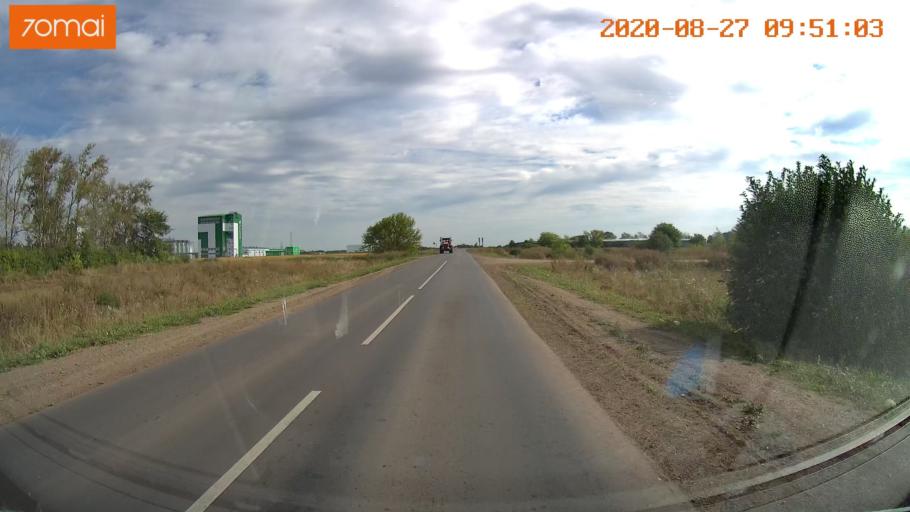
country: RU
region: Tula
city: Kurkino
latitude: 53.4151
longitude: 38.6276
